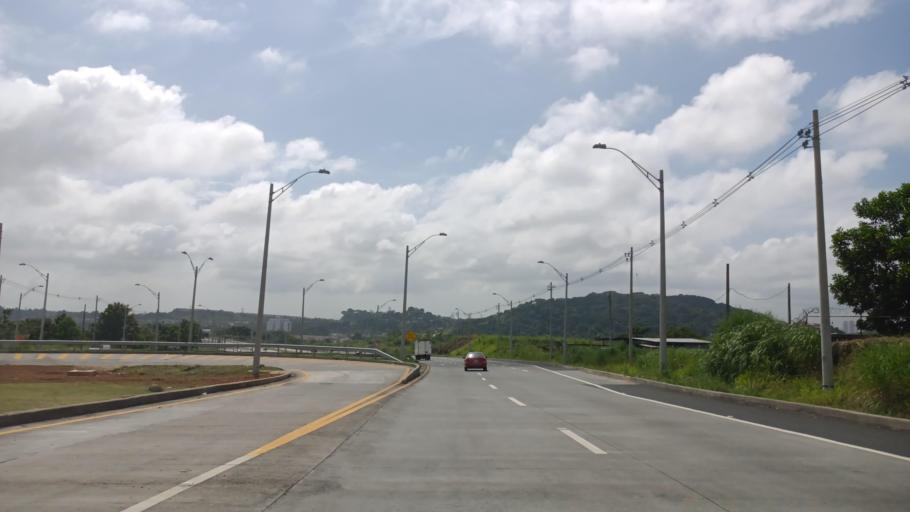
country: PA
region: Panama
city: San Miguelito
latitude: 9.0945
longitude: -79.4653
